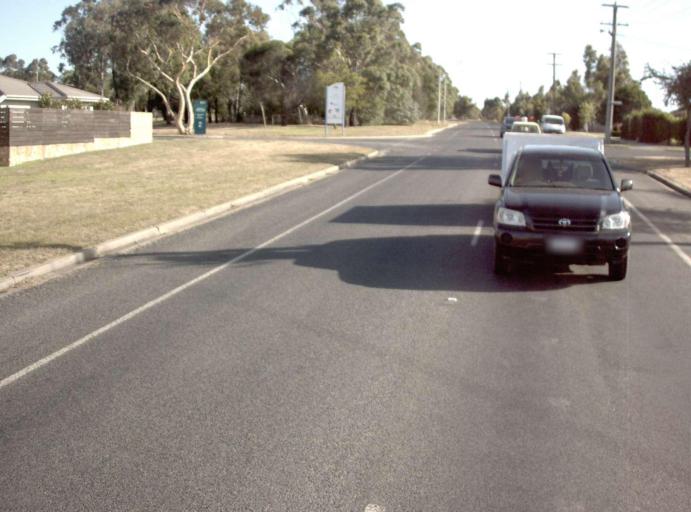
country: AU
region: Victoria
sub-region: Latrobe
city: Traralgon
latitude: -38.2094
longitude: 146.5203
